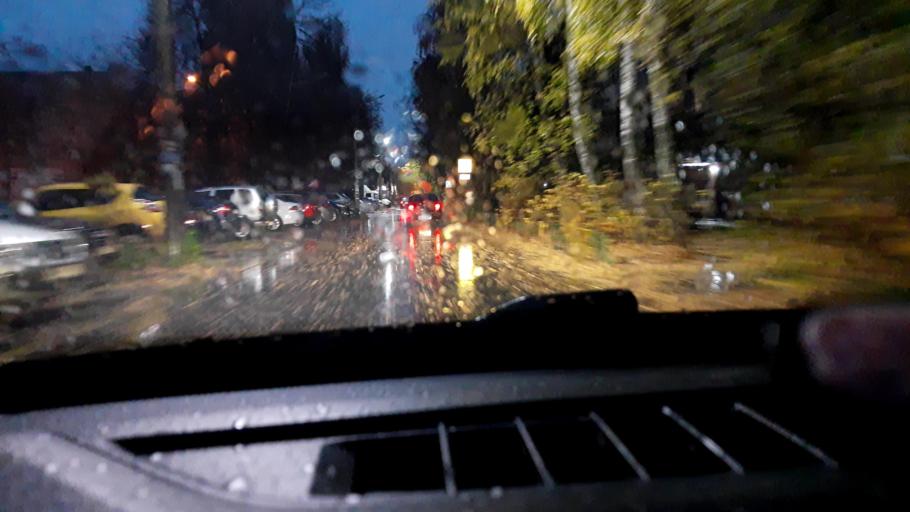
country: RU
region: Nizjnij Novgorod
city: Nizhniy Novgorod
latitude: 56.3159
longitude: 43.8758
